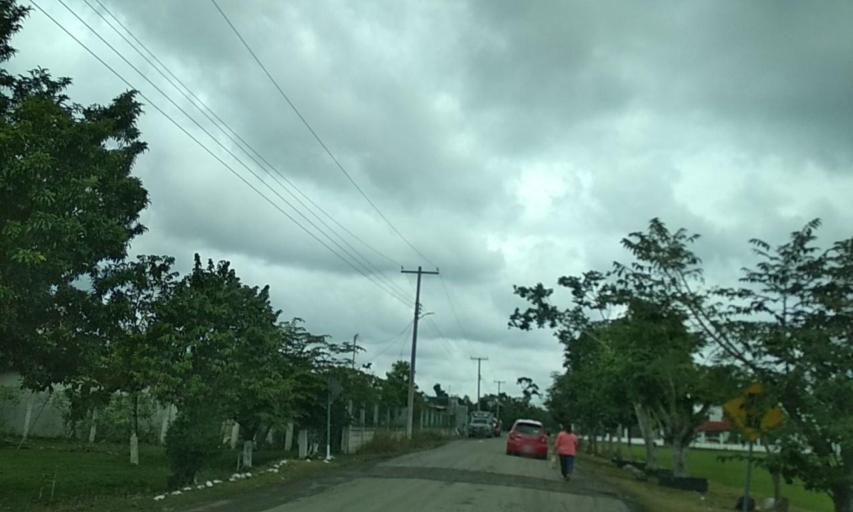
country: MX
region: Puebla
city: Espinal
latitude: 20.3240
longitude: -97.4182
